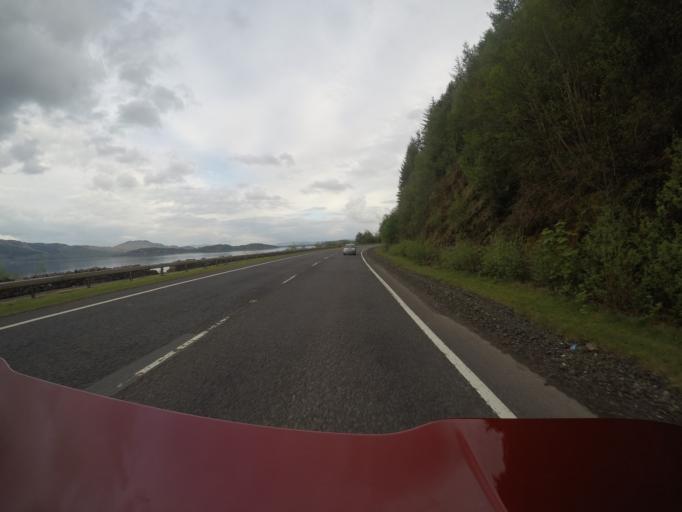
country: GB
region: Scotland
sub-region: West Dunbartonshire
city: Balloch
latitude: 56.1151
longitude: -4.6448
